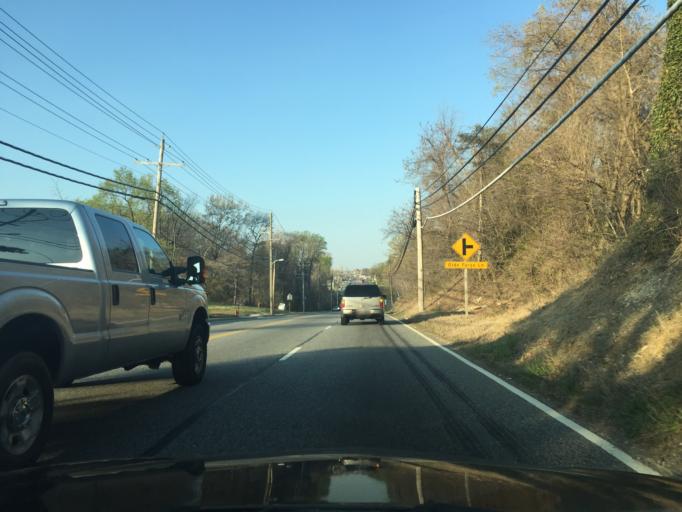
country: US
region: Maryland
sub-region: Baltimore County
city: Carney
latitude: 39.3858
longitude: -76.4959
